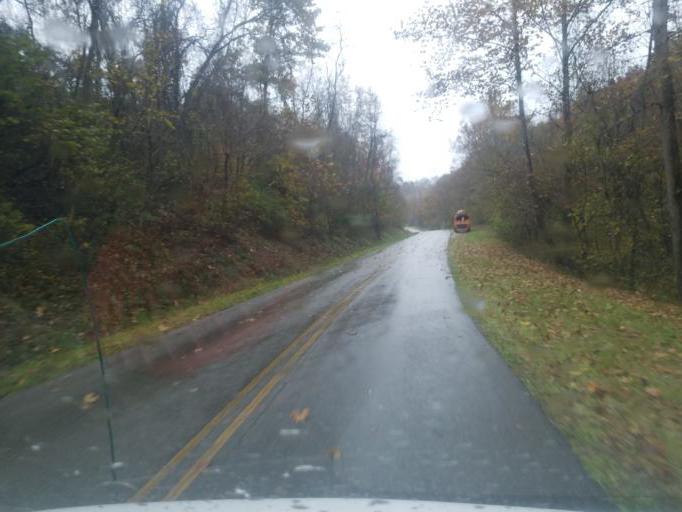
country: US
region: Ohio
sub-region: Washington County
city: Beverly
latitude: 39.4608
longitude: -81.6297
